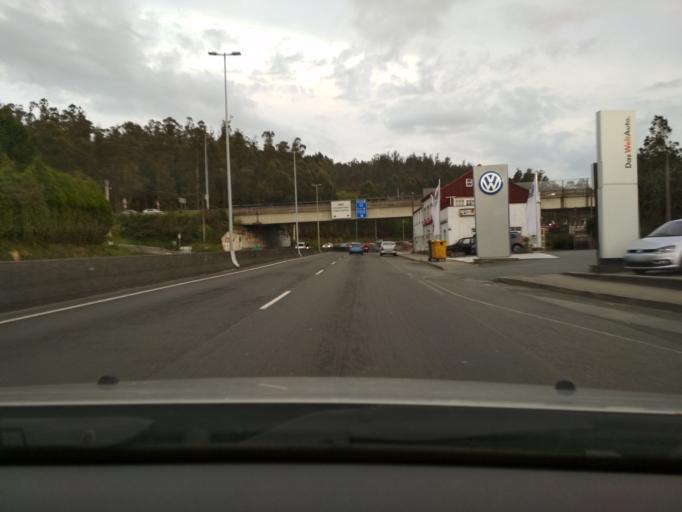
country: ES
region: Galicia
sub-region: Provincia da Coruna
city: Santiago de Compostela
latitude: 42.8573
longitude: -8.5715
